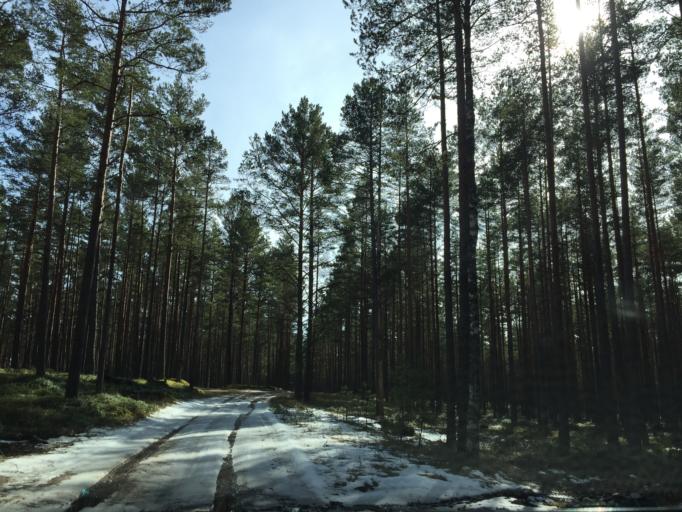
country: EE
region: Paernumaa
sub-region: Paernu linn
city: Parnu
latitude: 58.2355
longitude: 24.5189
